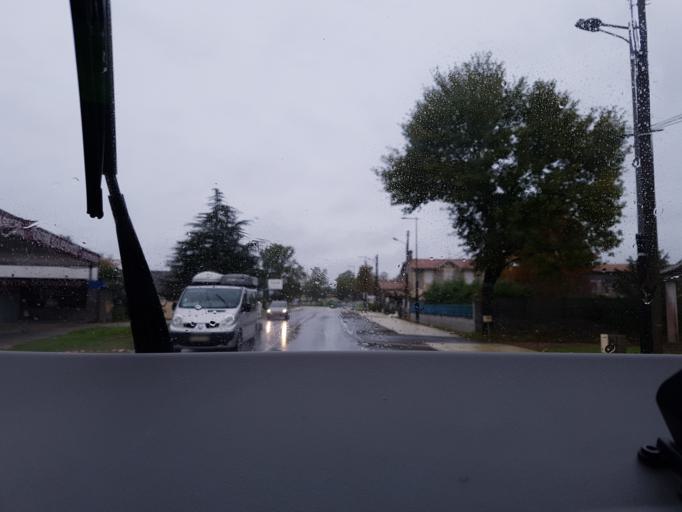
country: FR
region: Aquitaine
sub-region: Departement de la Gironde
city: Belin-Beliet
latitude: 44.5160
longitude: -0.7936
